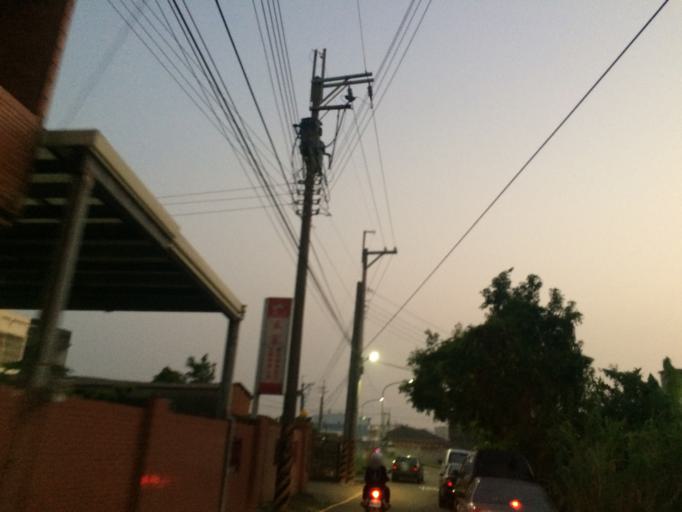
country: TW
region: Taiwan
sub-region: Hsinchu
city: Hsinchu
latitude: 24.7736
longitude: 120.9155
